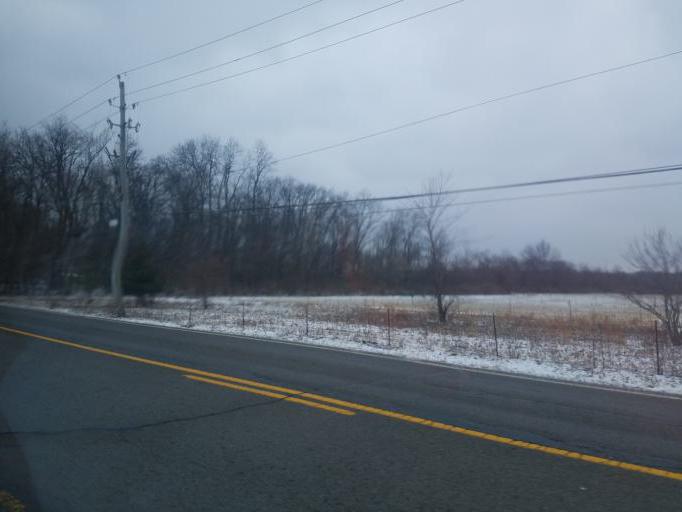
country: US
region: Ohio
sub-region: Franklin County
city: Reynoldsburg
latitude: 40.0039
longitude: -82.7909
